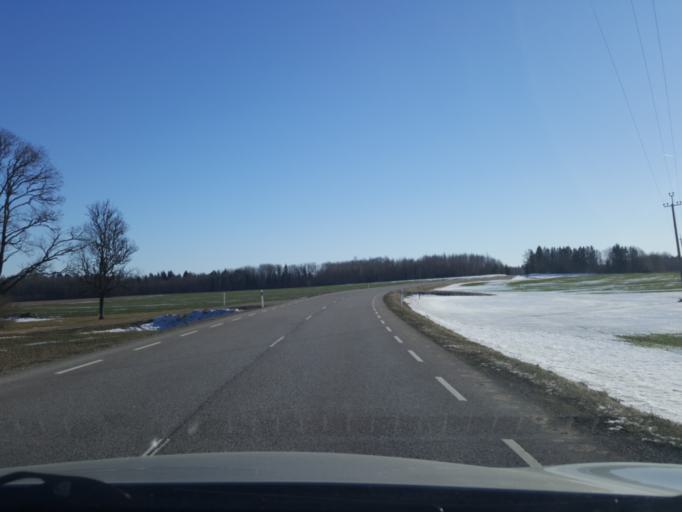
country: EE
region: Viljandimaa
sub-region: Vohma linn
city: Vohma
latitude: 58.5301
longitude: 25.6003
